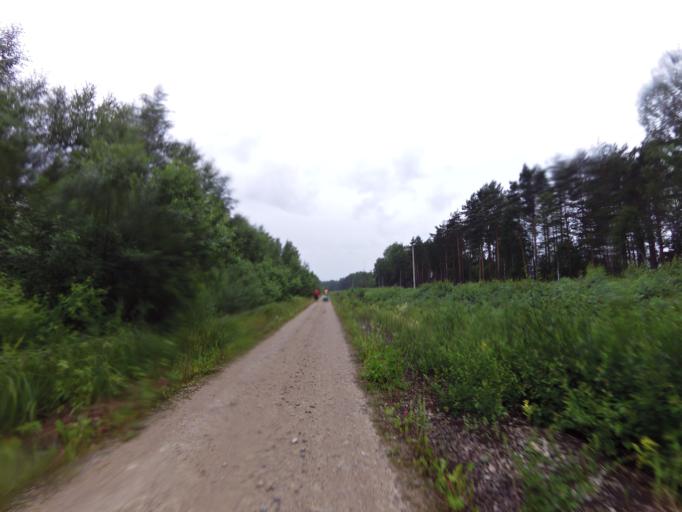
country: EE
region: Laeaene
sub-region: Lihula vald
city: Lihula
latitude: 58.9798
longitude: 23.9126
